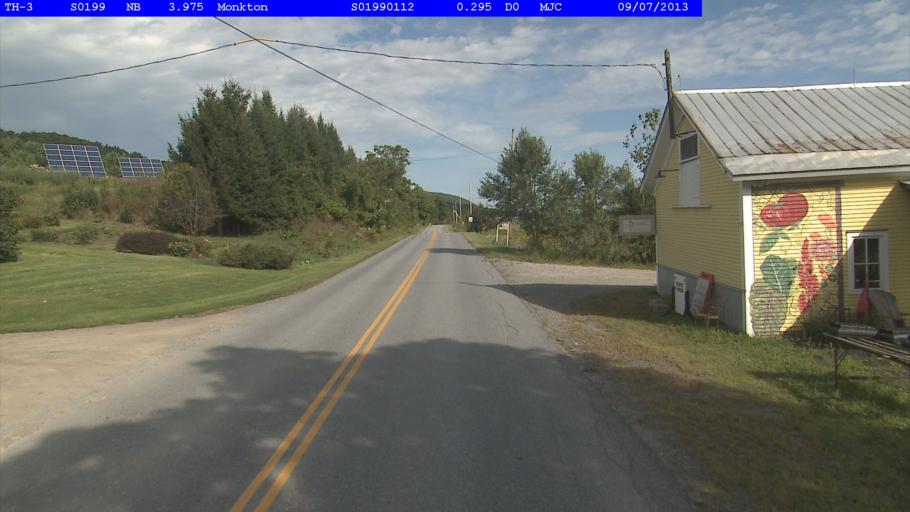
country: US
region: Vermont
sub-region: Addison County
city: Bristol
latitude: 44.1849
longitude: -73.1063
